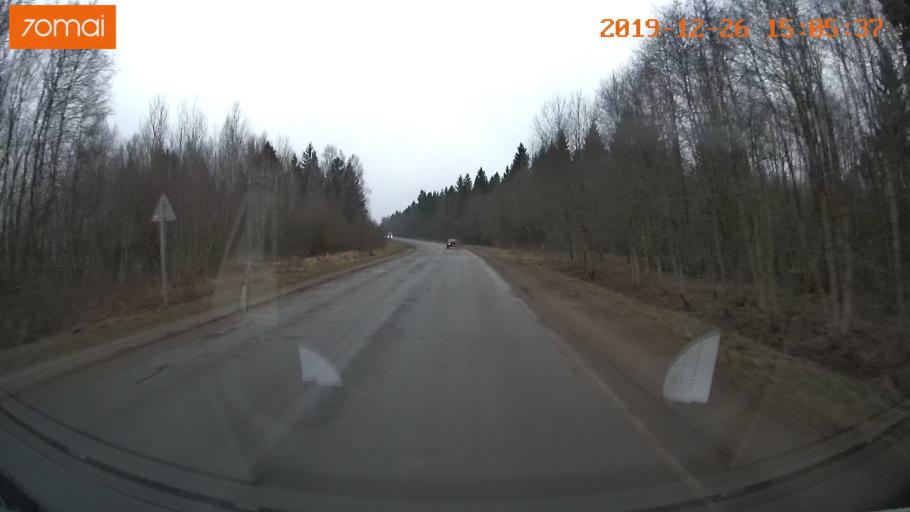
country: RU
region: Jaroslavl
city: Rybinsk
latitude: 58.1872
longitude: 38.8500
